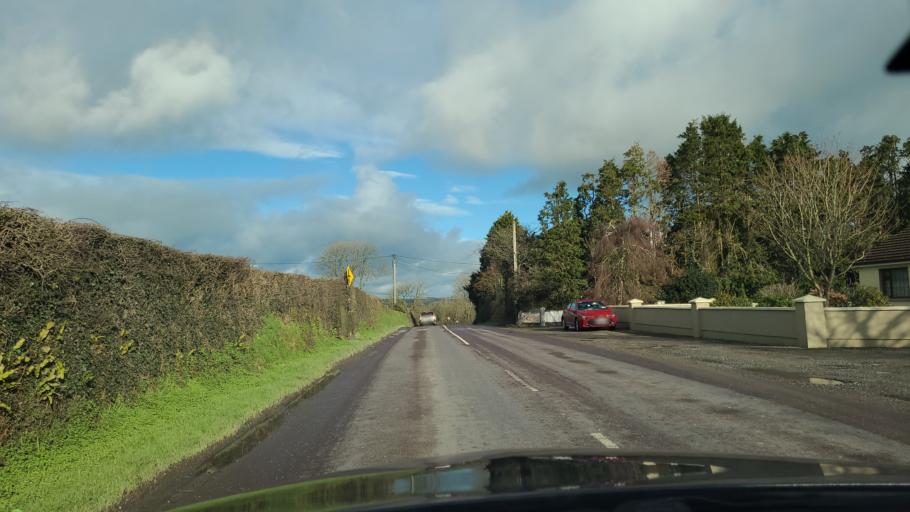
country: IE
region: Munster
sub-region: County Cork
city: Bandon
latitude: 51.7586
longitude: -8.7295
